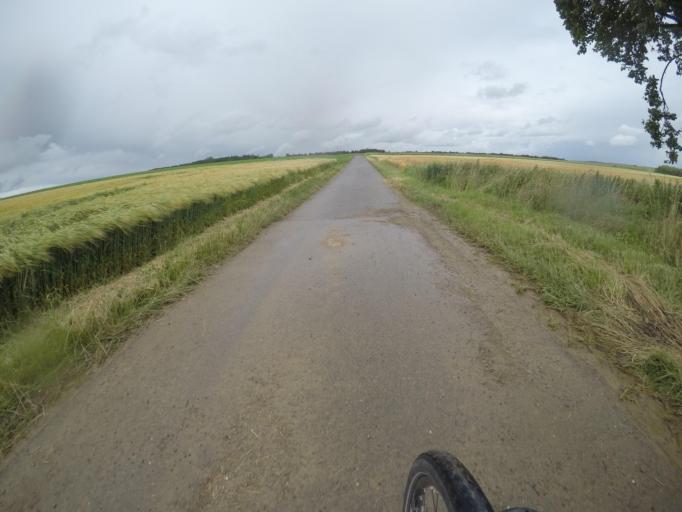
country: DE
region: Baden-Wuerttemberg
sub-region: Regierungsbezirk Stuttgart
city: Bondorf
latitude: 48.5598
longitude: 8.8284
